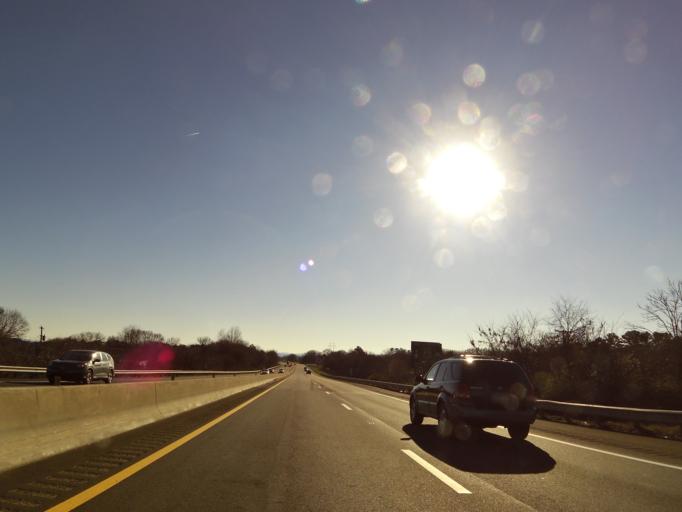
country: US
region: Tennessee
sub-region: Jefferson County
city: White Pine
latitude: 36.0391
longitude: -83.3322
